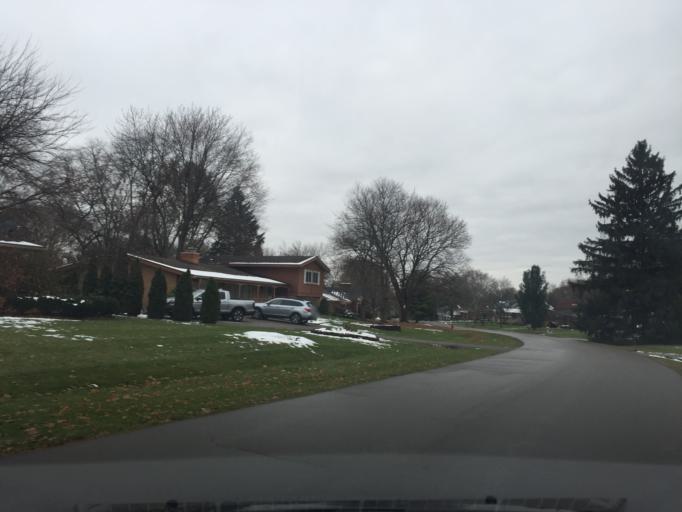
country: US
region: Michigan
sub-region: Oakland County
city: Franklin
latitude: 42.5387
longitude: -83.2901
